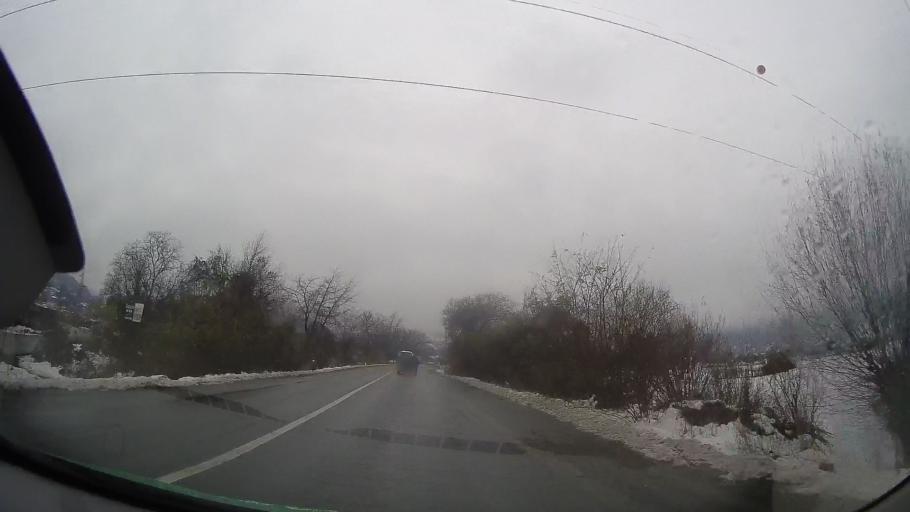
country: RO
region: Neamt
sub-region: Comuna Pangarati
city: Stejaru
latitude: 46.9189
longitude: 26.1889
